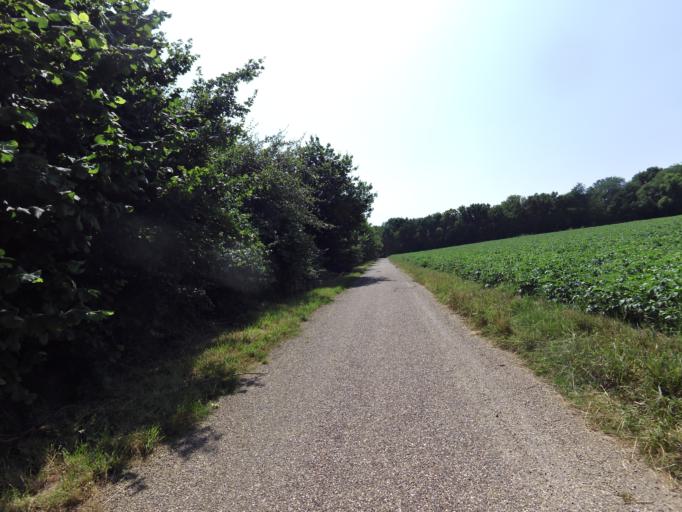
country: NL
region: Limburg
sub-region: Gemeente Kerkrade
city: Kerkrade
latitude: 50.8999
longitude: 6.0658
